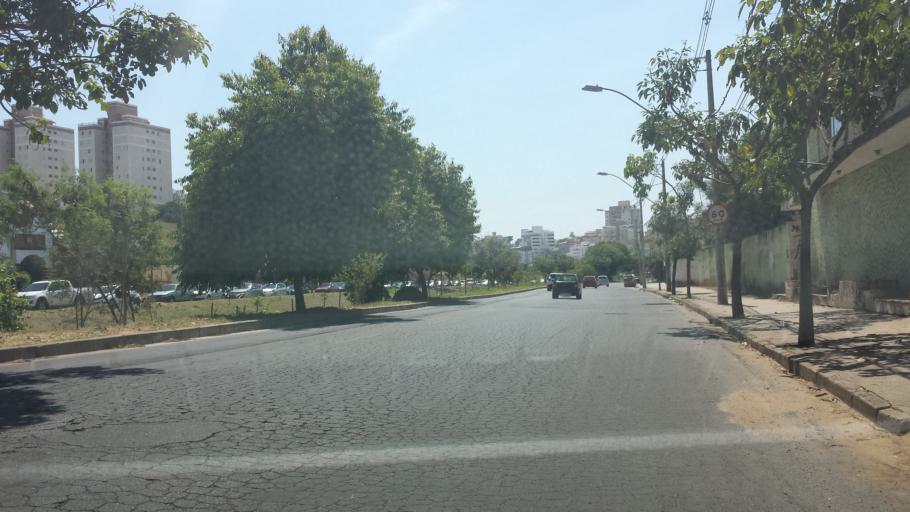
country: BR
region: Minas Gerais
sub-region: Belo Horizonte
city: Belo Horizonte
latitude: -19.8795
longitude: -43.9924
